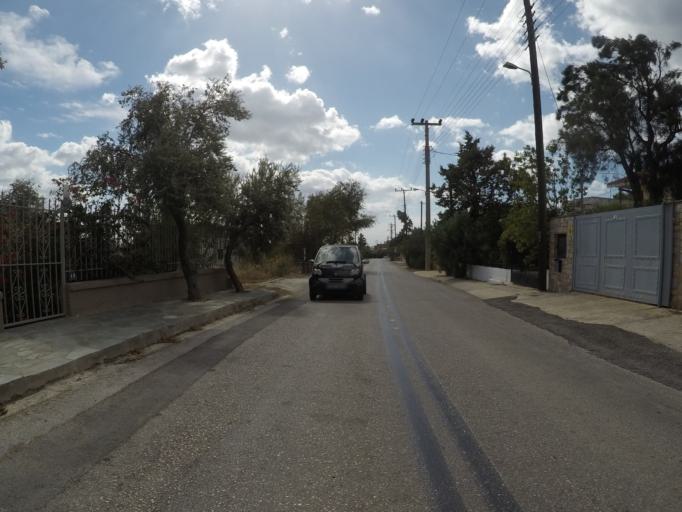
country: GR
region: Attica
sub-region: Nomarchia Anatolikis Attikis
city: Agios Dimitrios Kropias
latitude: 37.8051
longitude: 23.8667
